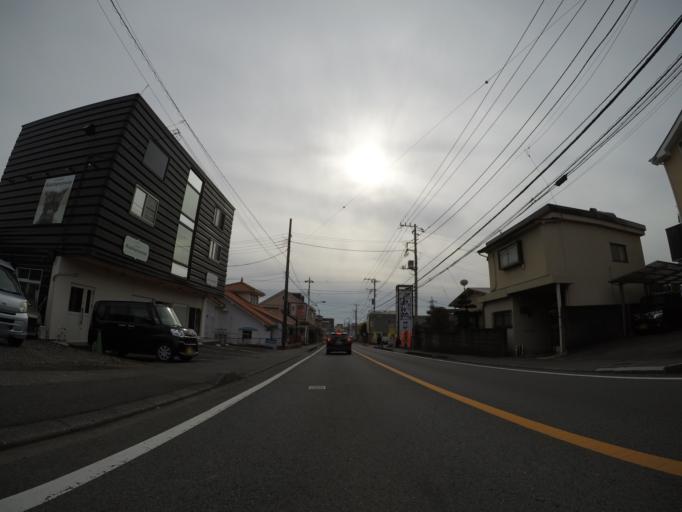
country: JP
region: Shizuoka
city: Fuji
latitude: 35.1748
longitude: 138.6822
